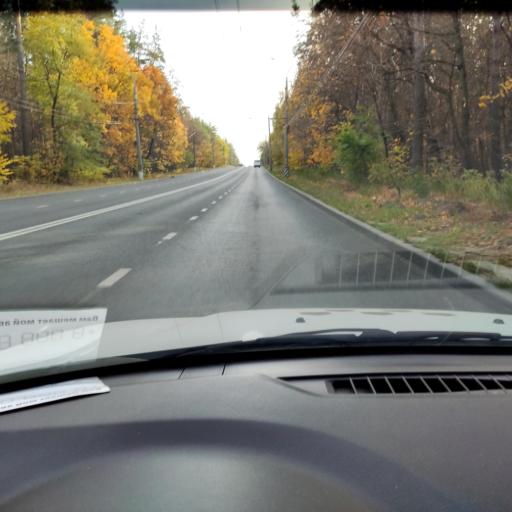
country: RU
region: Samara
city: Zhigulevsk
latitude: 53.4973
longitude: 49.4631
